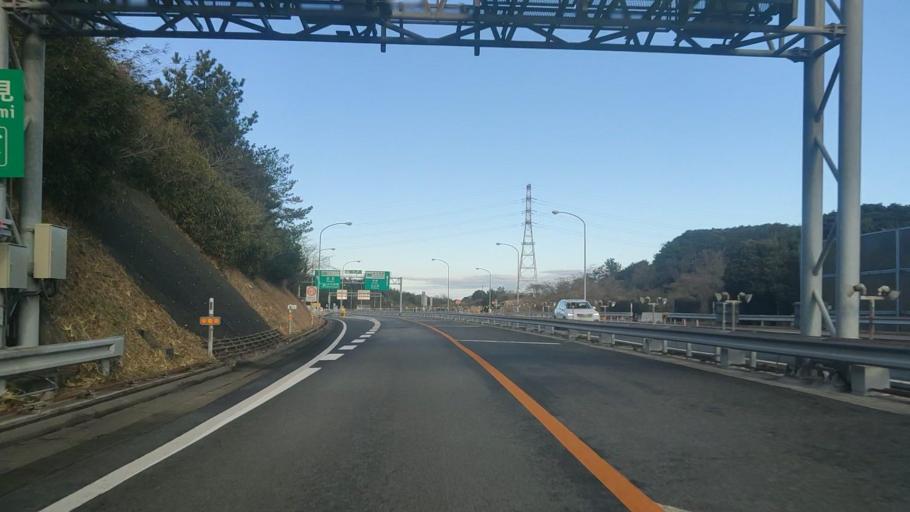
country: JP
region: Oita
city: Hiji
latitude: 33.3766
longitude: 131.4537
